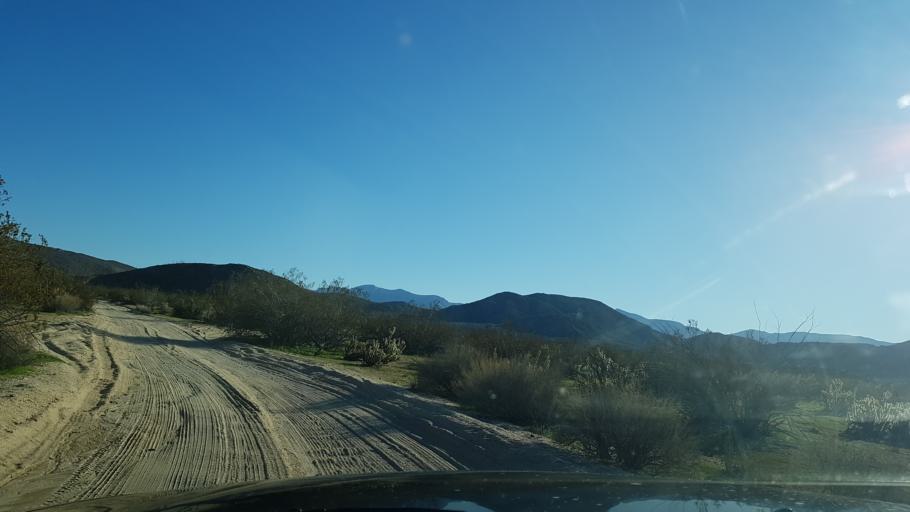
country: US
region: California
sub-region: San Diego County
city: Julian
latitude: 33.0218
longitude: -116.3952
